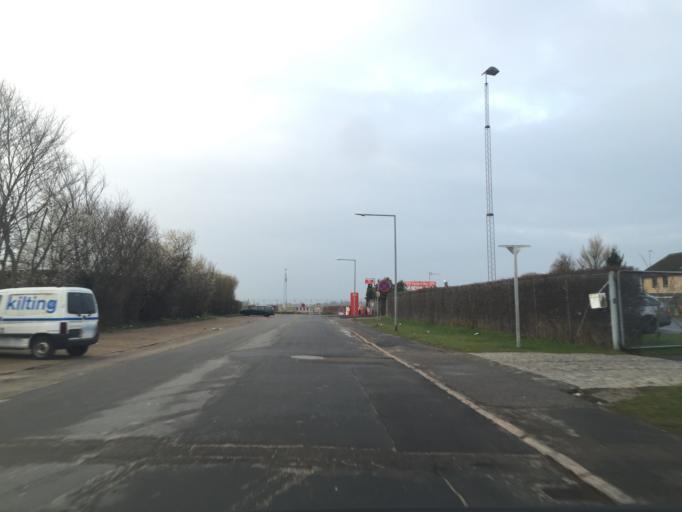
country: DK
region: Capital Region
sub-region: Tarnby Kommune
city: Tarnby
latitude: 55.6146
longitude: 12.6300
